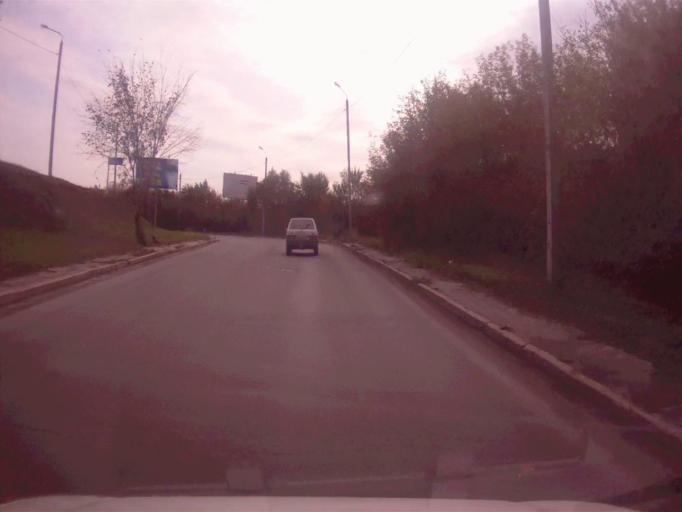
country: RU
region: Chelyabinsk
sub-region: Gorod Chelyabinsk
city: Chelyabinsk
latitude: 55.1605
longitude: 61.4283
